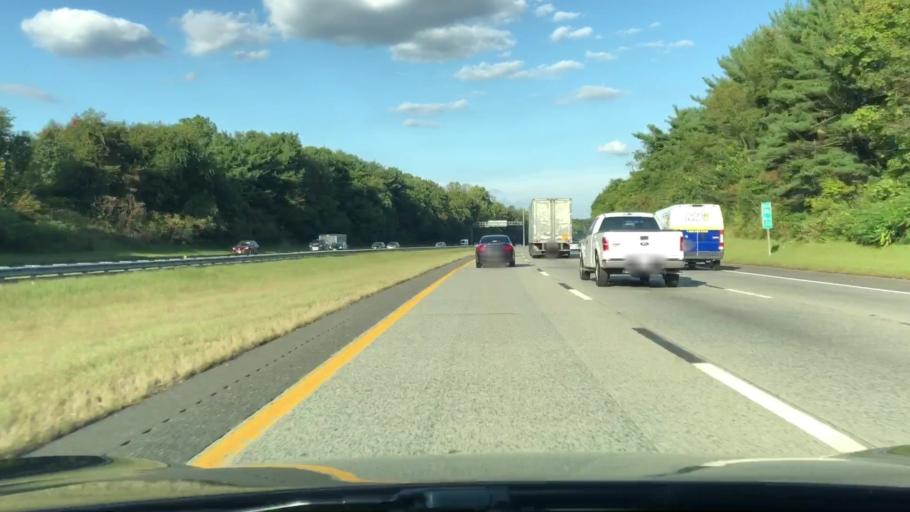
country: US
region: New Jersey
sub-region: Burlington County
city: Willingboro
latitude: 39.9839
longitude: -74.8911
